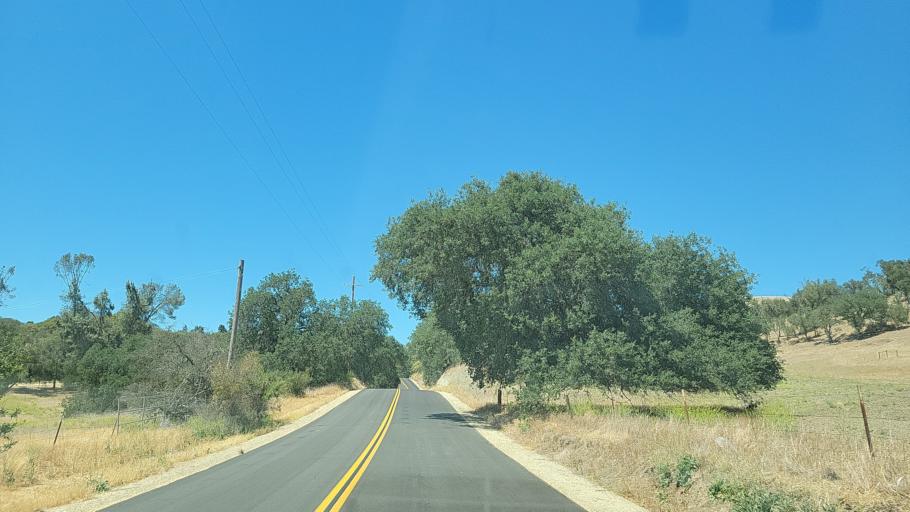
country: US
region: California
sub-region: San Luis Obispo County
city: Atascadero
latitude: 35.4731
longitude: -120.6235
